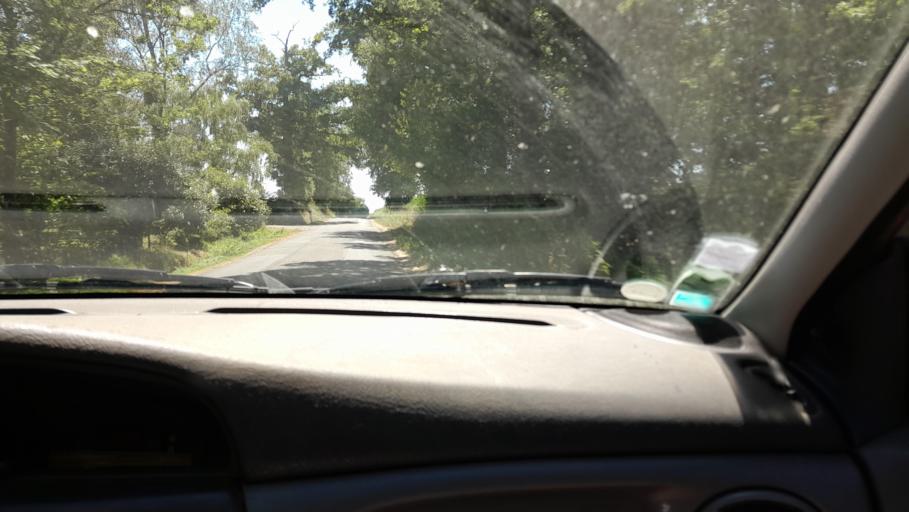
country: FR
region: Pays de la Loire
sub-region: Departement de la Mayenne
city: Congrier
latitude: 47.8218
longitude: -1.1965
